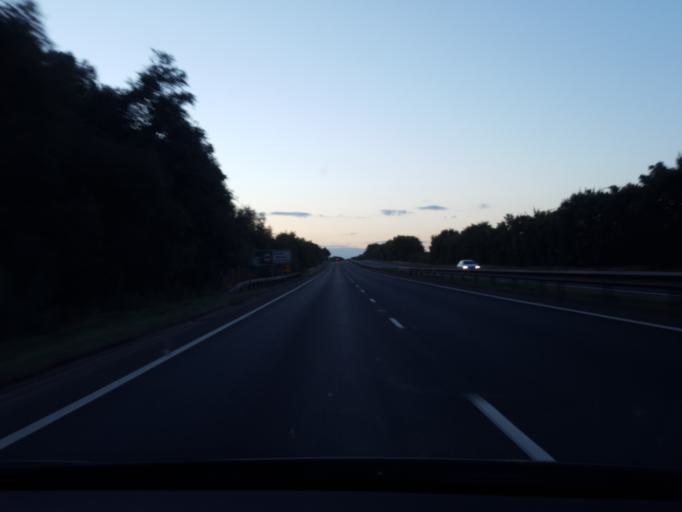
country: GB
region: England
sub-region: Leicestershire
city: Mountsorrel
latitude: 52.7289
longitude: -1.1321
